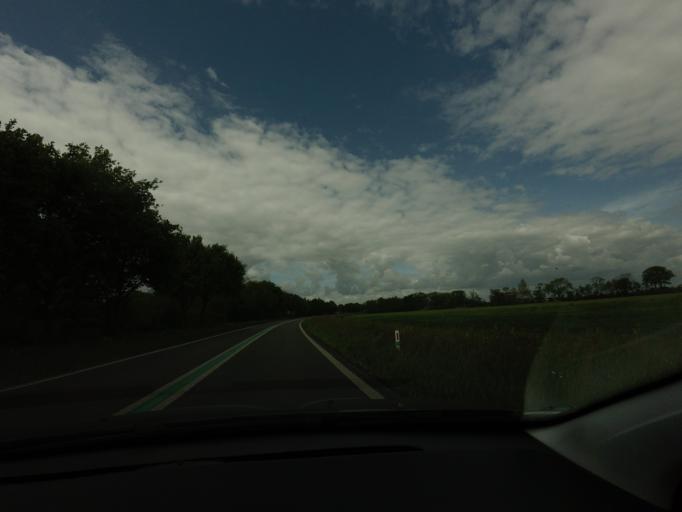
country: NL
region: Friesland
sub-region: Sudwest Fryslan
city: Koudum
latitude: 52.9075
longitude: 5.4553
